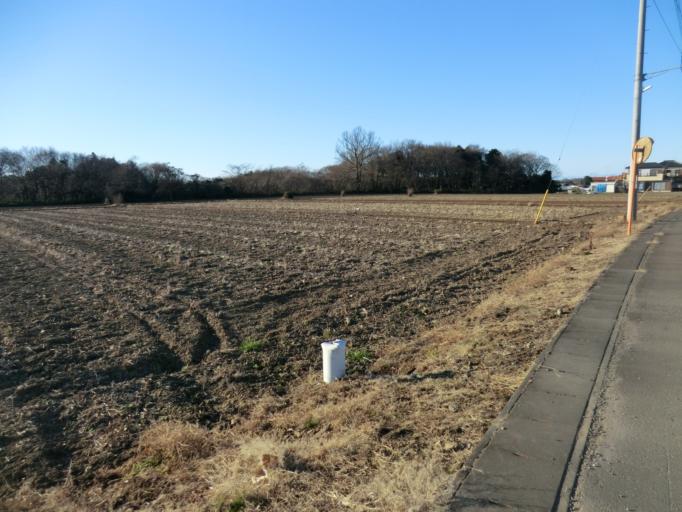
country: JP
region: Ibaraki
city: Mitsukaido
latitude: 36.0562
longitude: 139.9683
